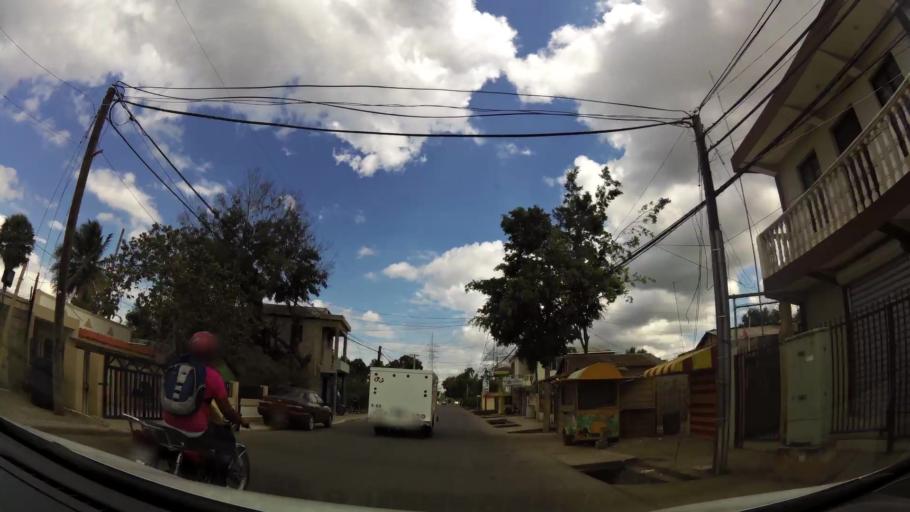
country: DO
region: Santiago
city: Licey al Medio
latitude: 19.4018
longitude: -70.6548
